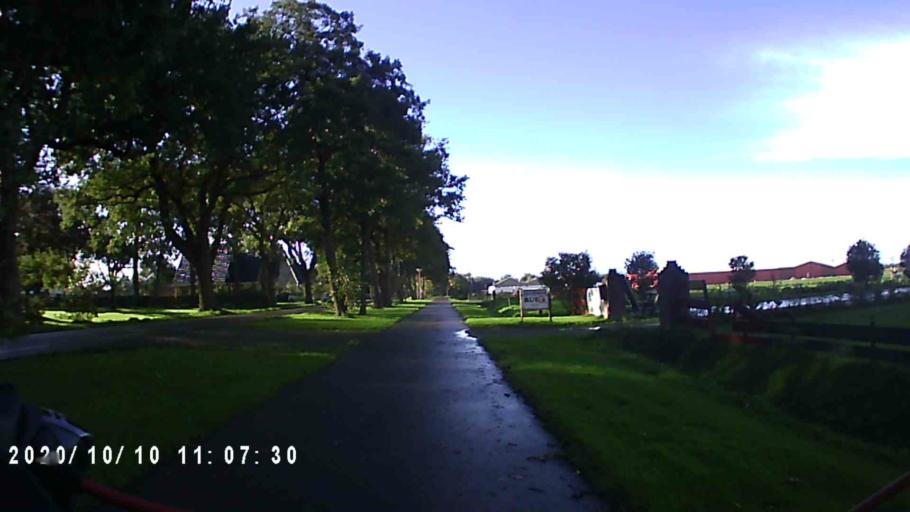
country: NL
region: Friesland
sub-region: Gemeente Smallingerland
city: Drachtstercompagnie
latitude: 53.1233
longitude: 6.2140
